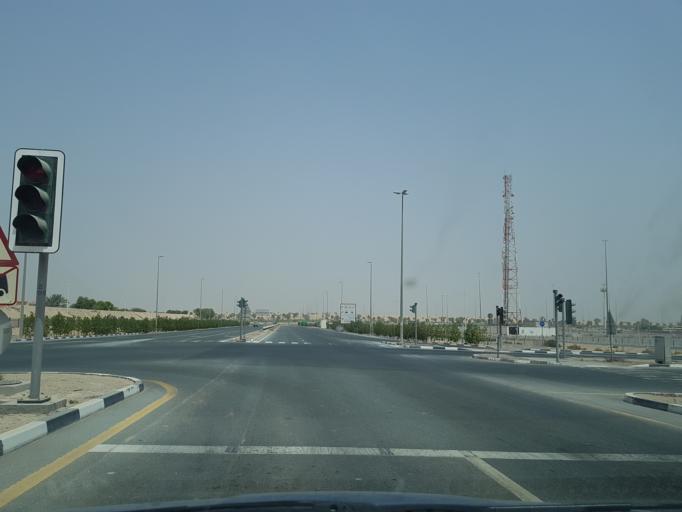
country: AE
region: Dubai
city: Dubai
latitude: 25.0600
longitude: 55.2999
